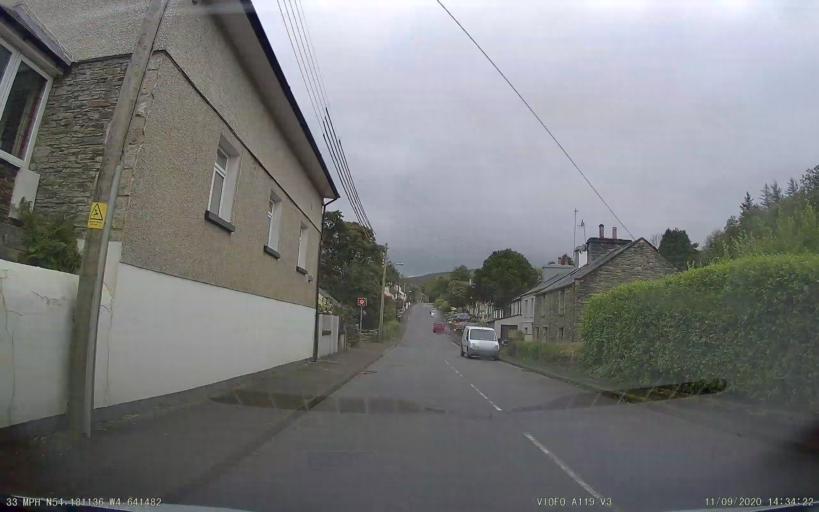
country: IM
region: Castletown
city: Castletown
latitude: 54.1812
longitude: -4.6415
